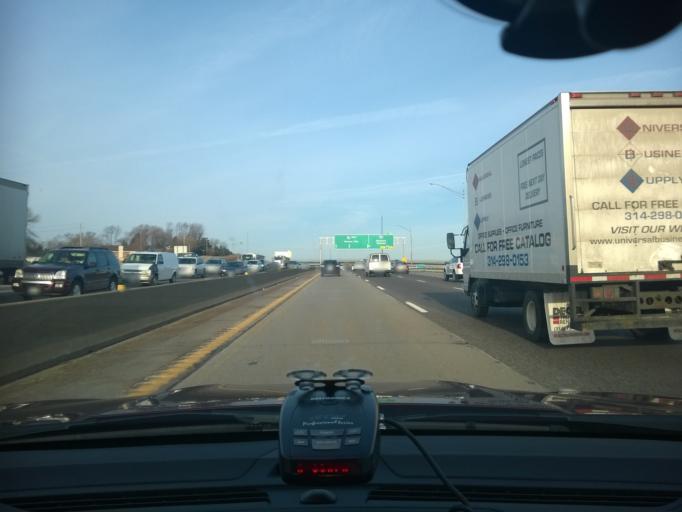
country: US
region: Missouri
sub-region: Saint Louis County
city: Bridgeton
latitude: 38.7459
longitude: -90.4309
